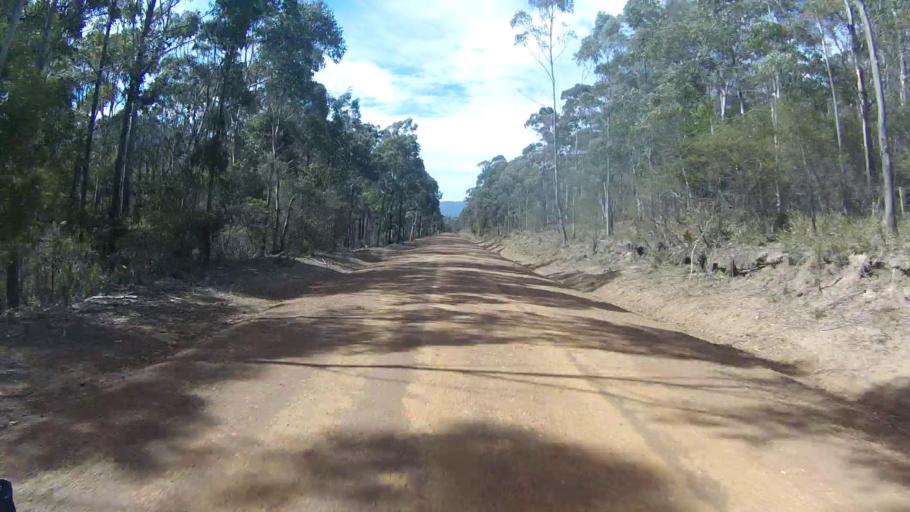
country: AU
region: Tasmania
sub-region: Sorell
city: Sorell
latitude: -42.6168
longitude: 147.9003
